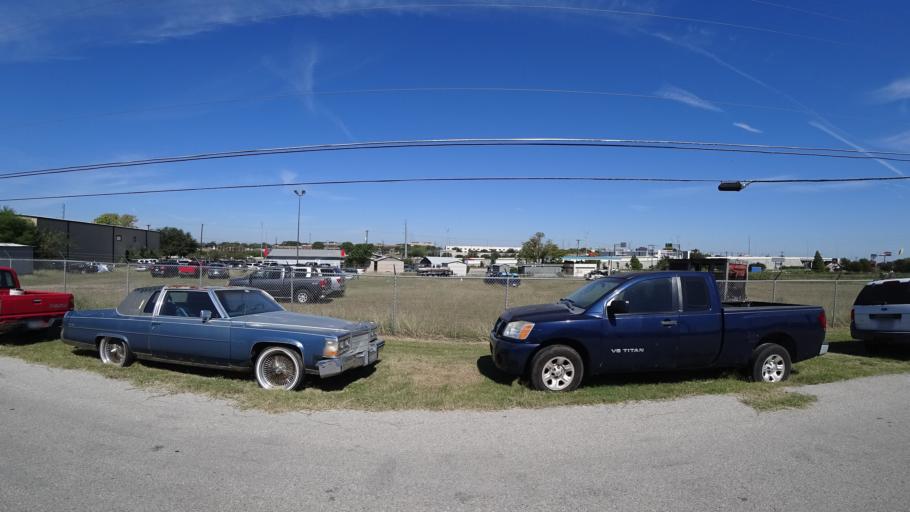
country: US
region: Texas
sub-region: Travis County
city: Austin
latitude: 30.2115
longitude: -97.7169
